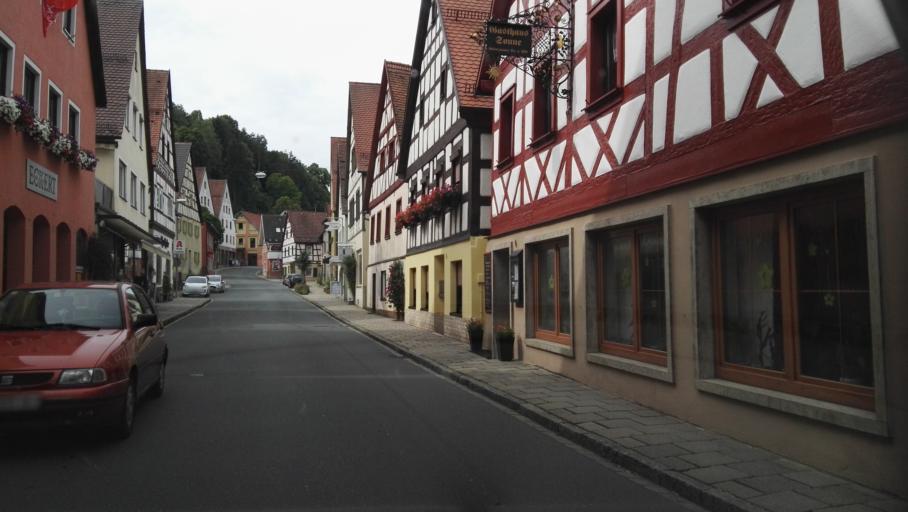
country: DE
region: Bavaria
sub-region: Upper Franconia
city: Waischenfeld
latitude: 49.8454
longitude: 11.3447
